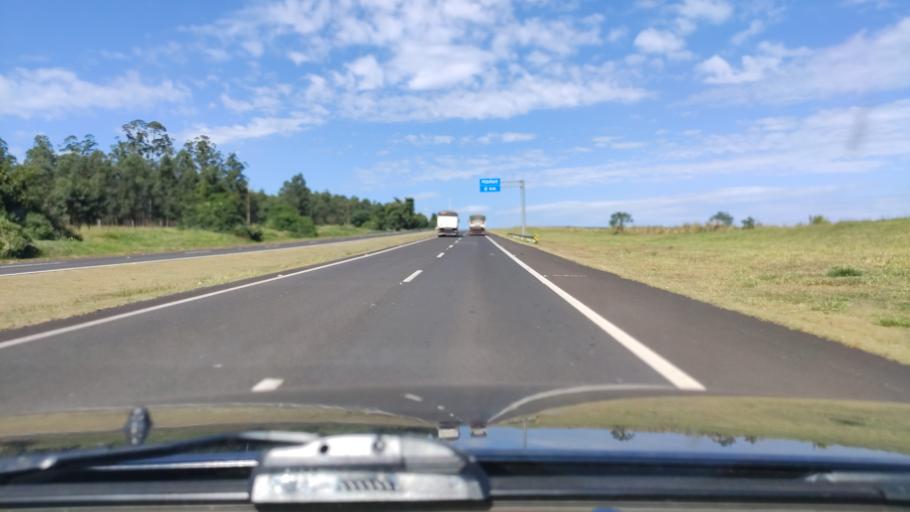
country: BR
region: Sao Paulo
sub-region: Rancharia
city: Rancharia
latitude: -22.4240
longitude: -51.0278
